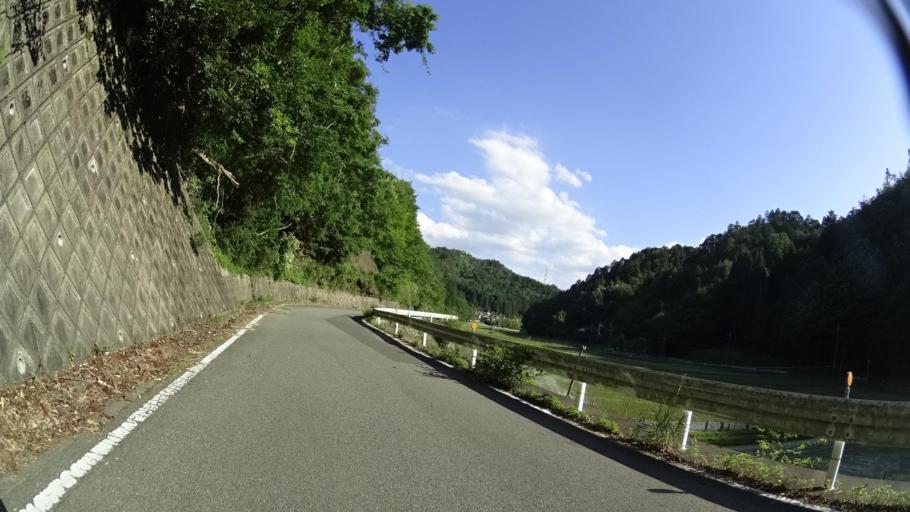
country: JP
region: Kyoto
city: Kameoka
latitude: 34.9704
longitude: 135.5619
